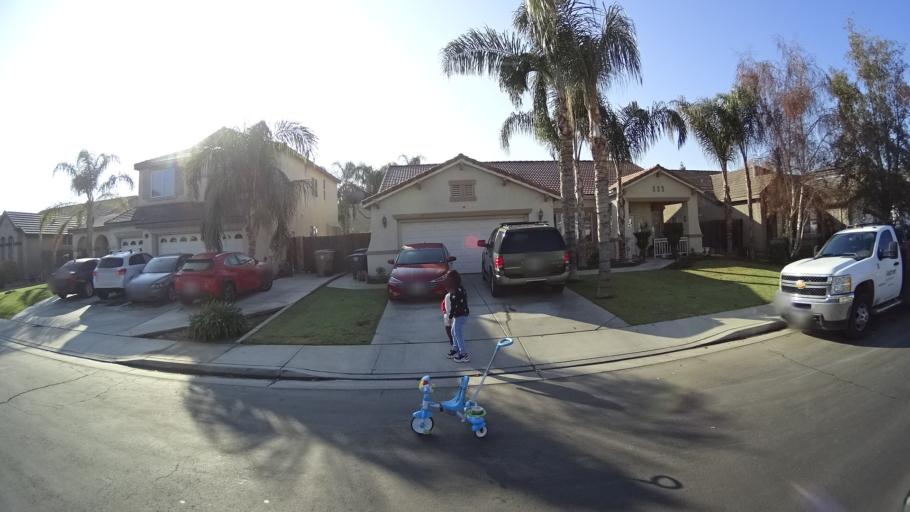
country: US
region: California
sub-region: Kern County
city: Greenacres
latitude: 35.3103
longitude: -119.1225
